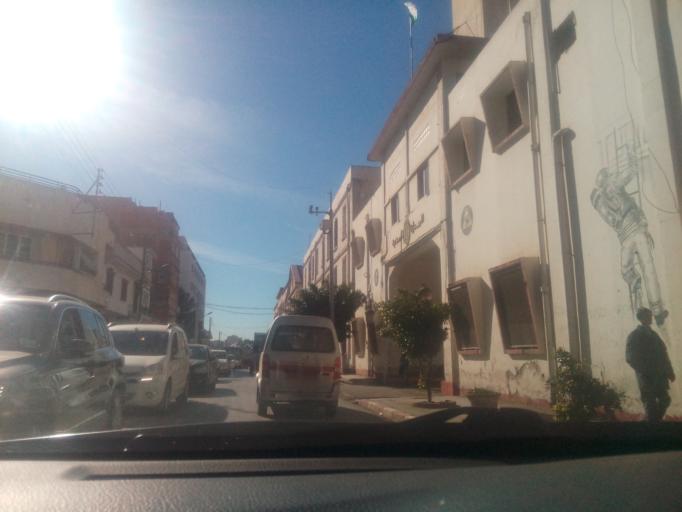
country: DZ
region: Oran
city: Oran
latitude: 35.6949
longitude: -0.6440
